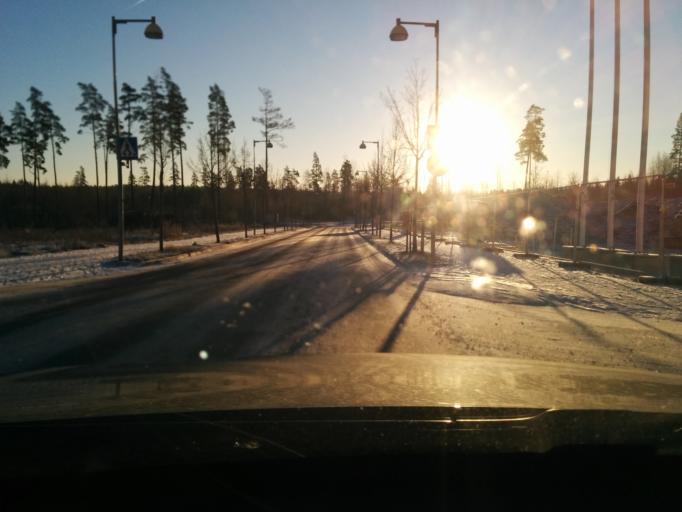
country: SE
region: Stockholm
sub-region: Vallentuna Kommun
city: Vallentuna
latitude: 59.4988
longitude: 18.0900
